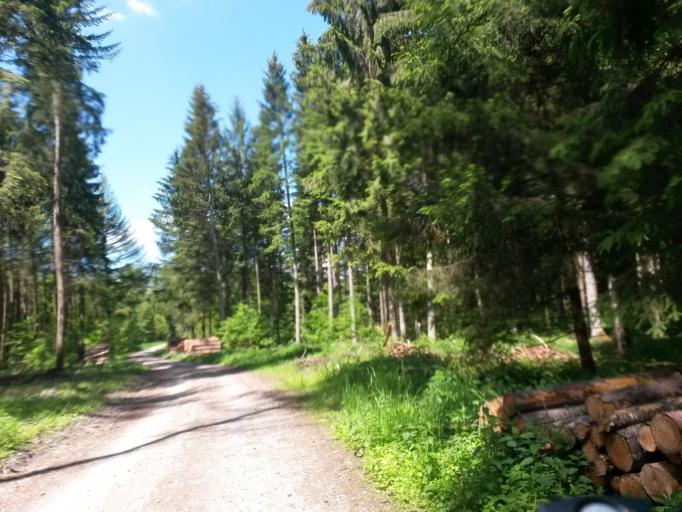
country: DE
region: Baden-Wuerttemberg
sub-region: Tuebingen Region
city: Aulendorf
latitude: 47.9452
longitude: 9.6961
